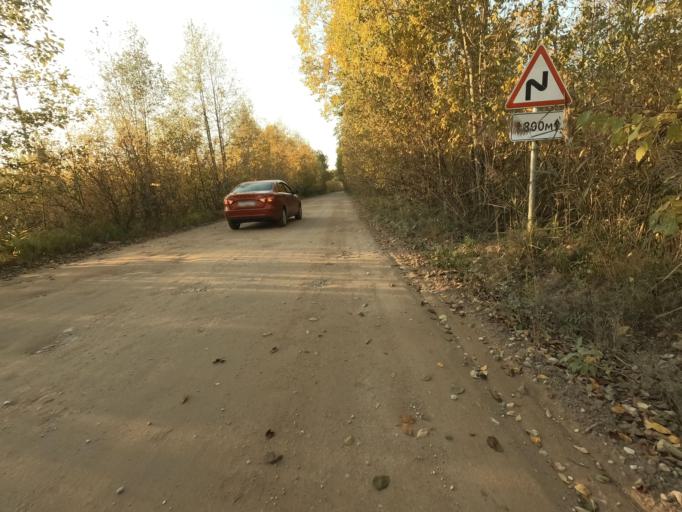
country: RU
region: Leningrad
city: Lyuban'
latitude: 59.0005
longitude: 31.1006
